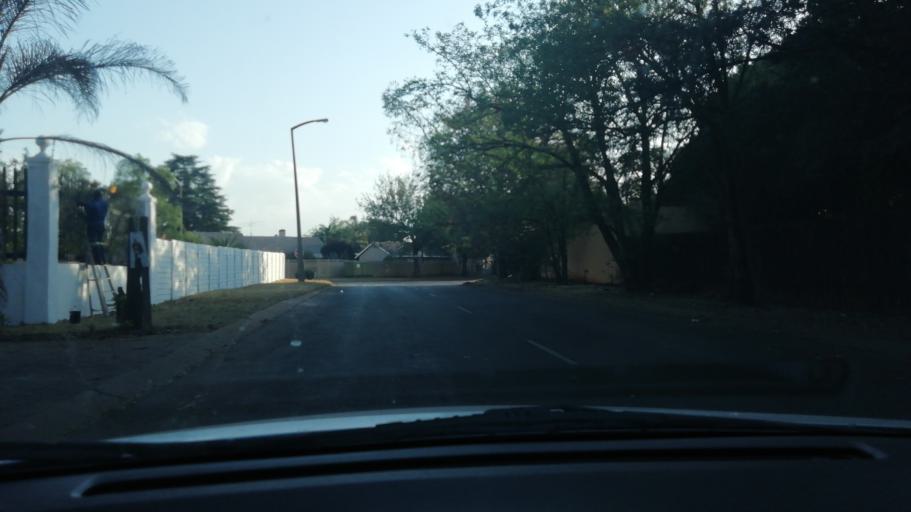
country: ZA
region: Gauteng
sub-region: Ekurhuleni Metropolitan Municipality
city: Benoni
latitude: -26.1995
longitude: 28.2947
